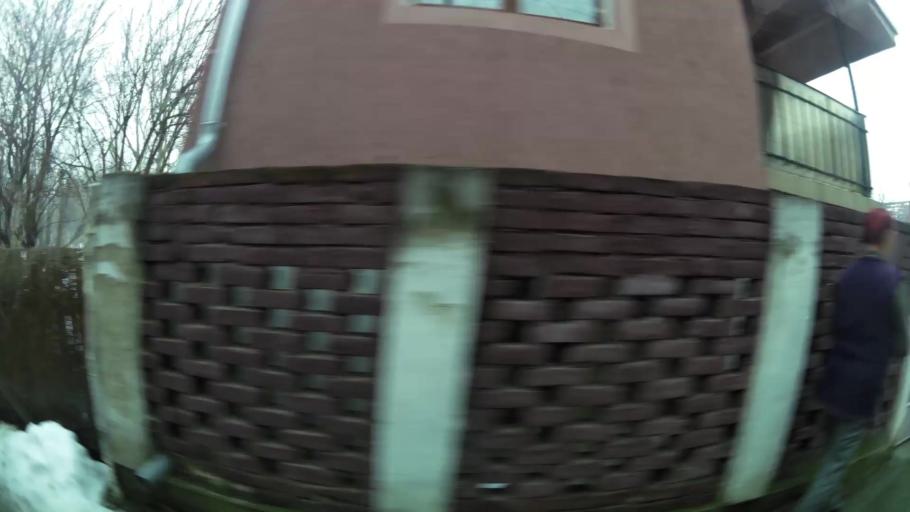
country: RS
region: Central Serbia
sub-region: Belgrade
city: Zvezdara
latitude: 44.7784
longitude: 20.5049
